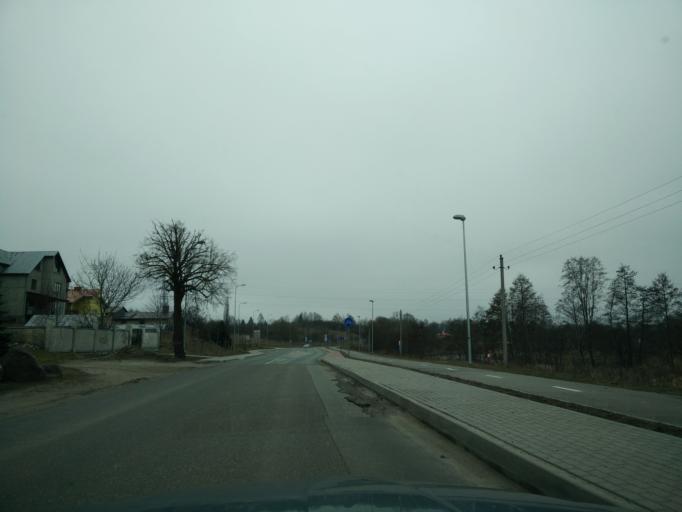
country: LT
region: Klaipedos apskritis
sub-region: Klaipeda
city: Klaipeda
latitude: 55.7199
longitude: 21.1694
